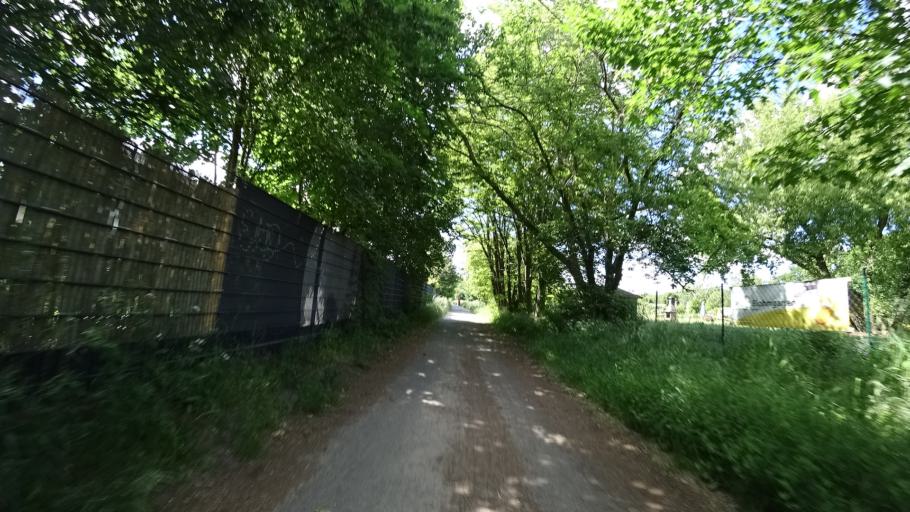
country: DE
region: Berlin
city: Lichtenrade
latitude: 52.3905
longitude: 13.3808
